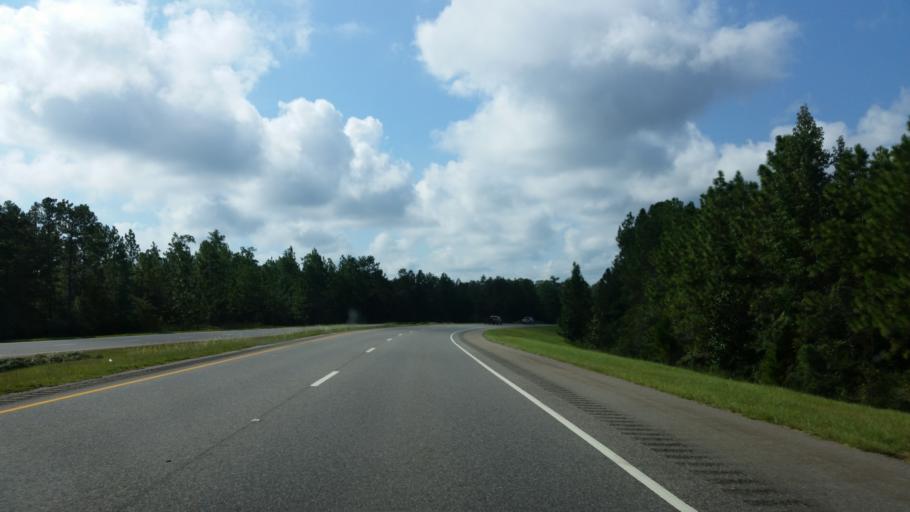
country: US
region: Alabama
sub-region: Baldwin County
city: Bay Minette
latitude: 30.9288
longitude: -87.7696
